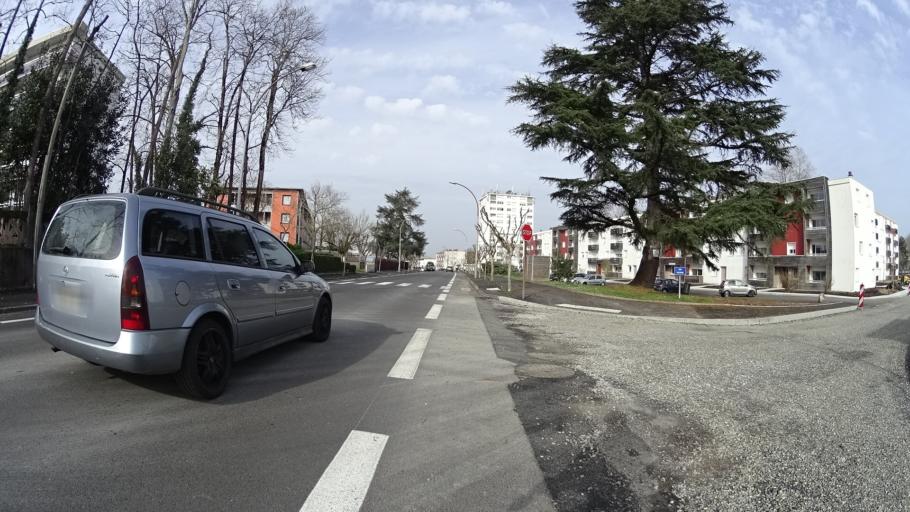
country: FR
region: Aquitaine
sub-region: Departement des Landes
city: Dax
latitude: 43.7009
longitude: -1.0541
